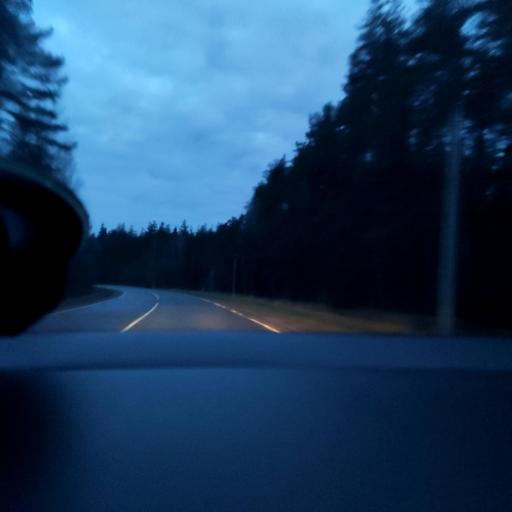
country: RU
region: Moskovskaya
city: Shaturtorf
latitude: 55.4490
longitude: 39.4372
